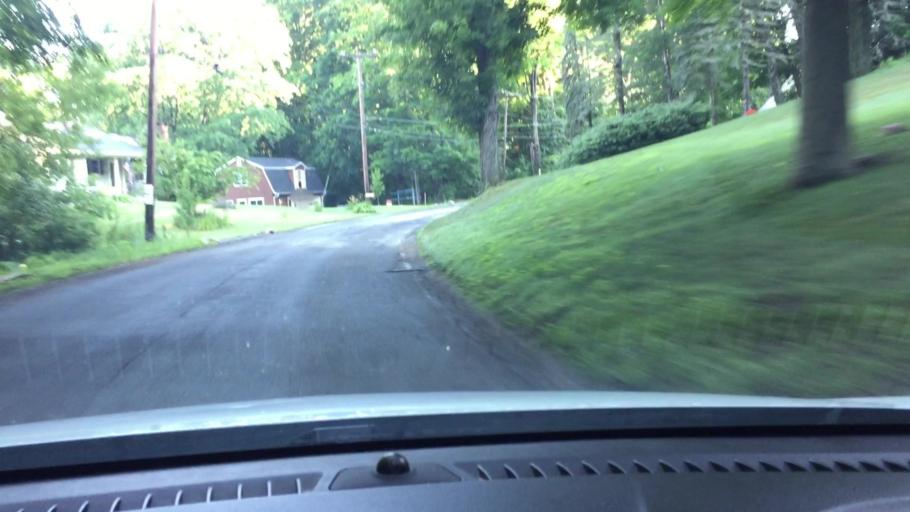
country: US
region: Massachusetts
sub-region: Berkshire County
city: Pittsfield
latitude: 42.4078
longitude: -73.2328
